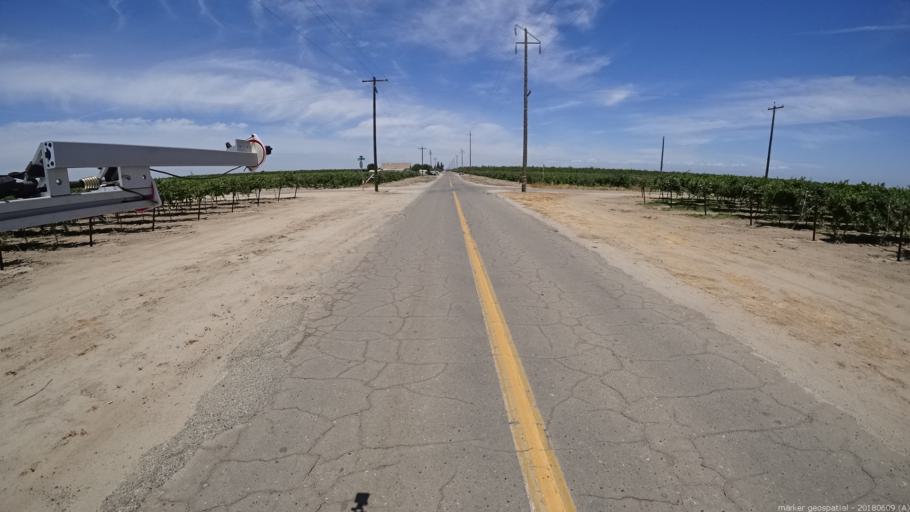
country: US
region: California
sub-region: Fresno County
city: Biola
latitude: 36.8437
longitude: -120.1103
